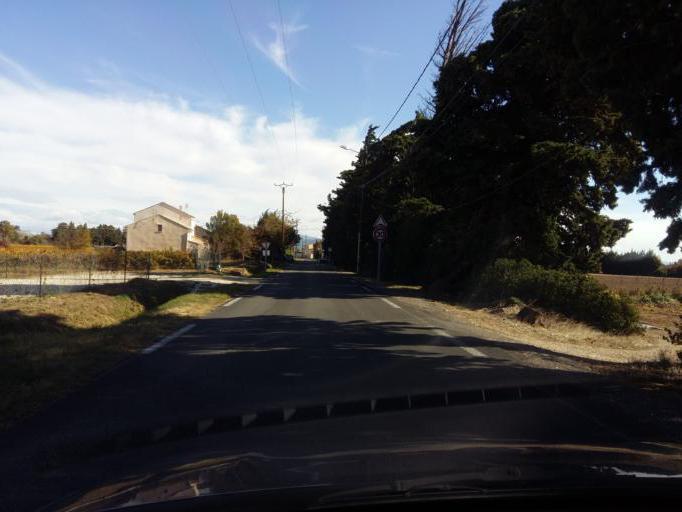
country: FR
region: Provence-Alpes-Cote d'Azur
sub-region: Departement du Vaucluse
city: Camaret-sur-Aigues
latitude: 44.1729
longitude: 4.8634
